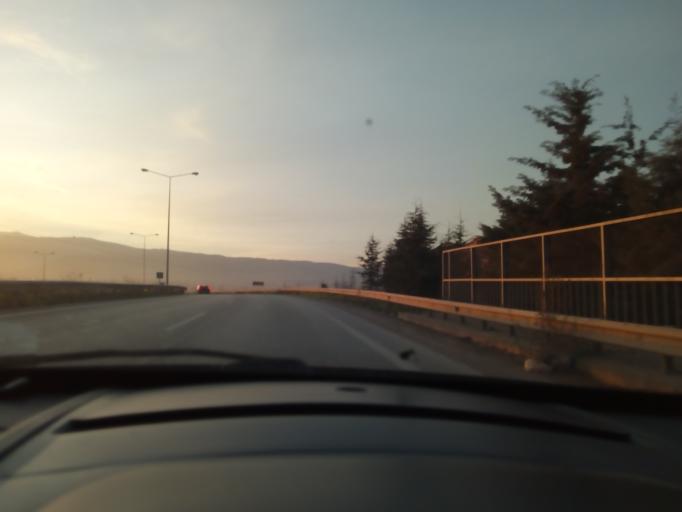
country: TR
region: Bursa
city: Niluefer
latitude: 40.2623
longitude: 28.9436
